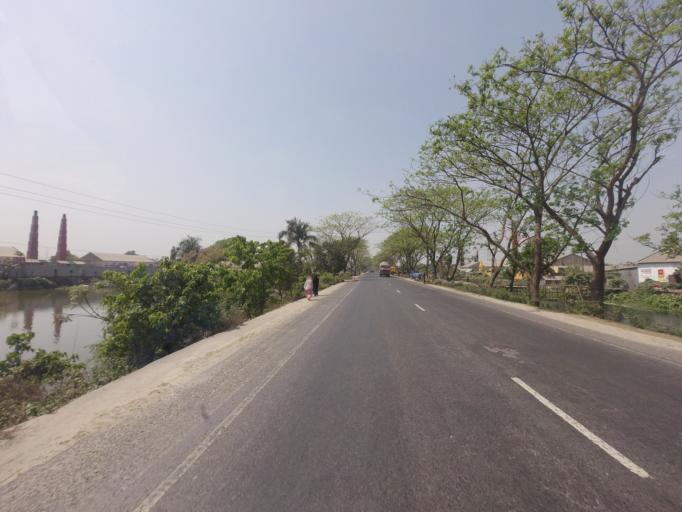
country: BD
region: Dhaka
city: Bhairab Bazar
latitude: 24.0432
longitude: 91.0548
